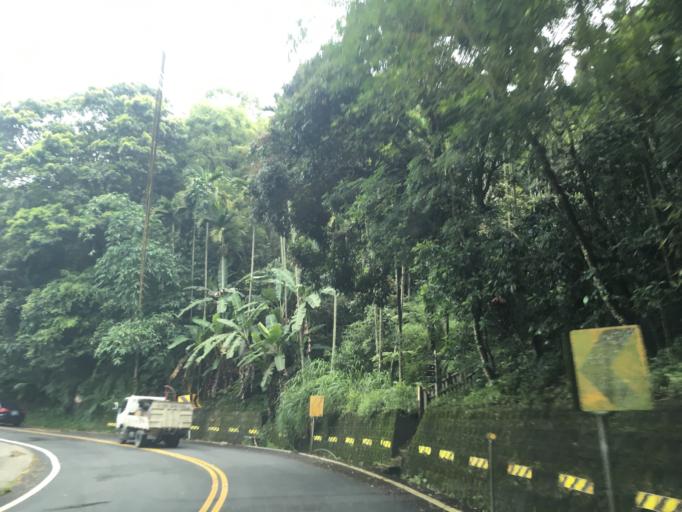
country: TW
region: Taiwan
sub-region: Yunlin
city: Douliu
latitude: 23.5587
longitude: 120.5871
